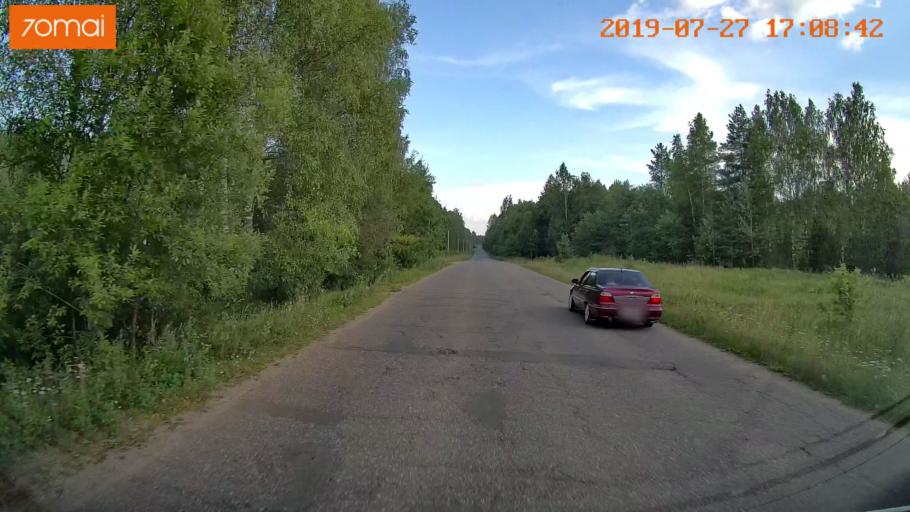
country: RU
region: Ivanovo
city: Novo-Talitsy
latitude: 57.0806
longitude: 40.8404
